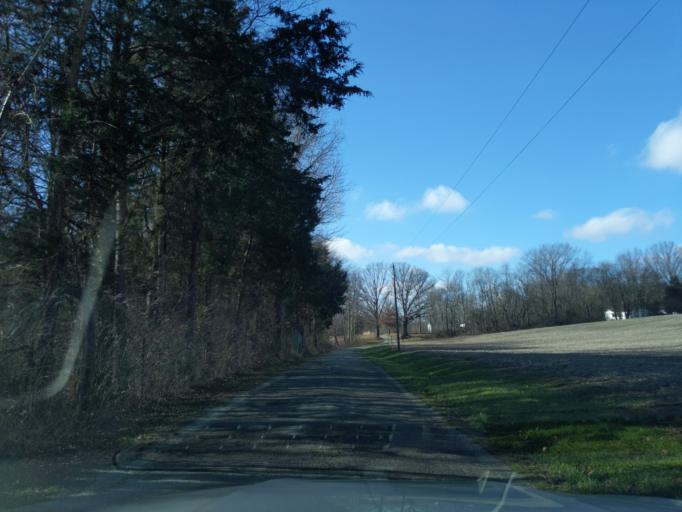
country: US
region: Indiana
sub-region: Decatur County
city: Greensburg
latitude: 39.2412
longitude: -85.4586
